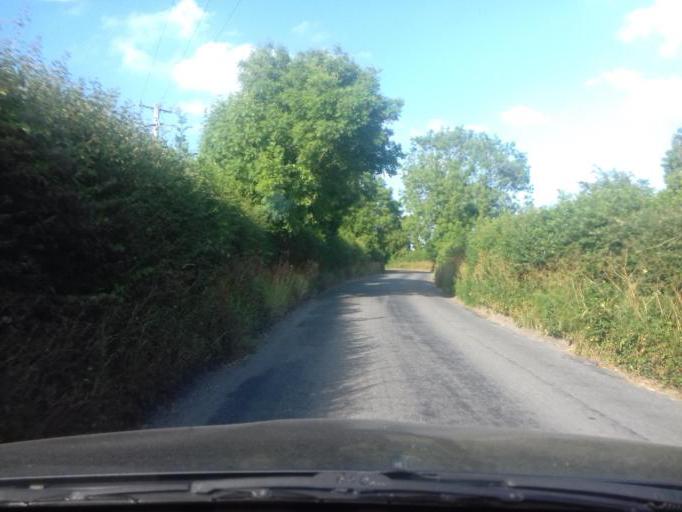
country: IE
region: Leinster
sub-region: An Mhi
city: Dunboyne
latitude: 53.4419
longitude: -6.4438
